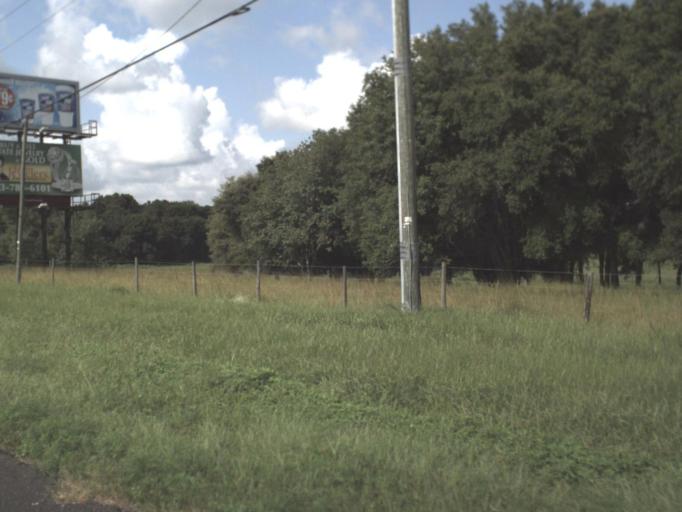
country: US
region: Florida
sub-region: Pasco County
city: Dade City
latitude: 28.3185
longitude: -82.1877
